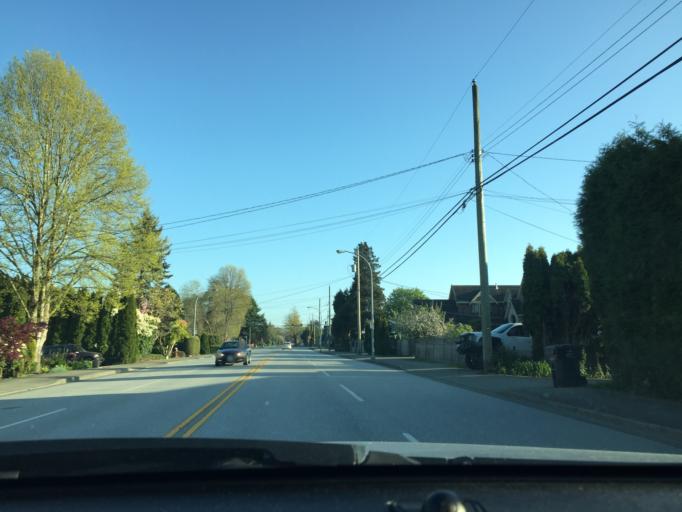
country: CA
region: British Columbia
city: Richmond
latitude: 49.1499
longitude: -123.1253
